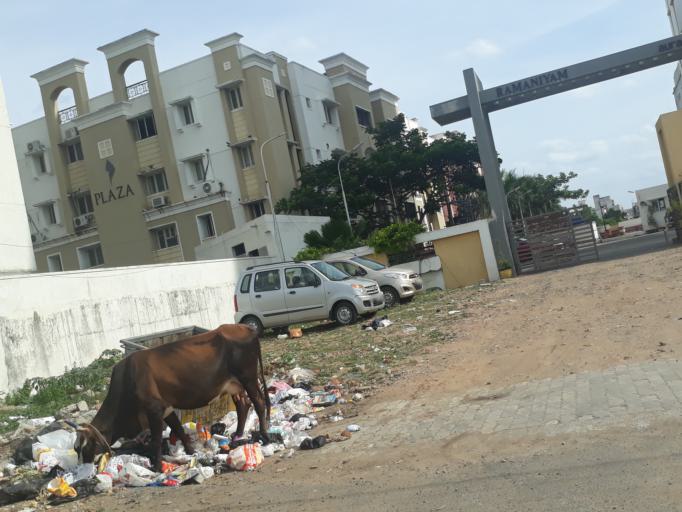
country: IN
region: Tamil Nadu
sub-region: Kancheepuram
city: Perungudi
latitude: 12.9499
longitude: 80.2332
